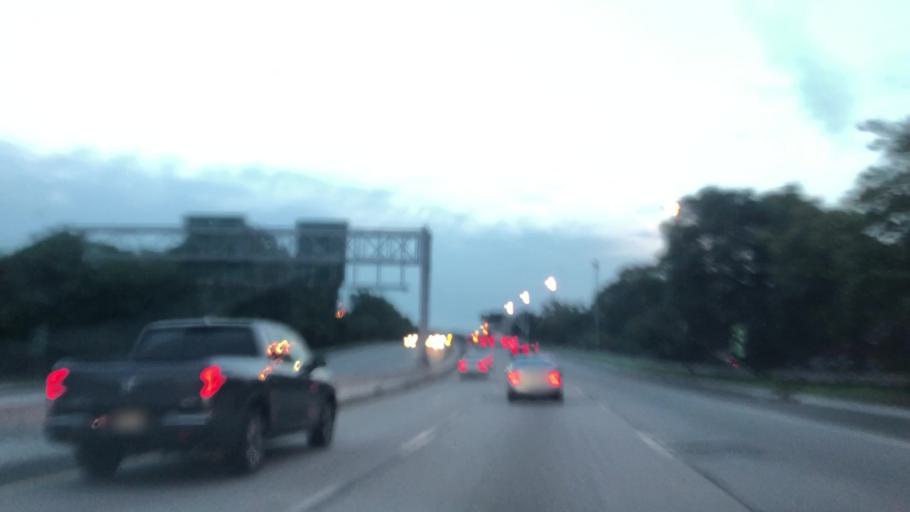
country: US
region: New Jersey
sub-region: Bergen County
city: Wallington
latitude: 40.8365
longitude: -74.1250
